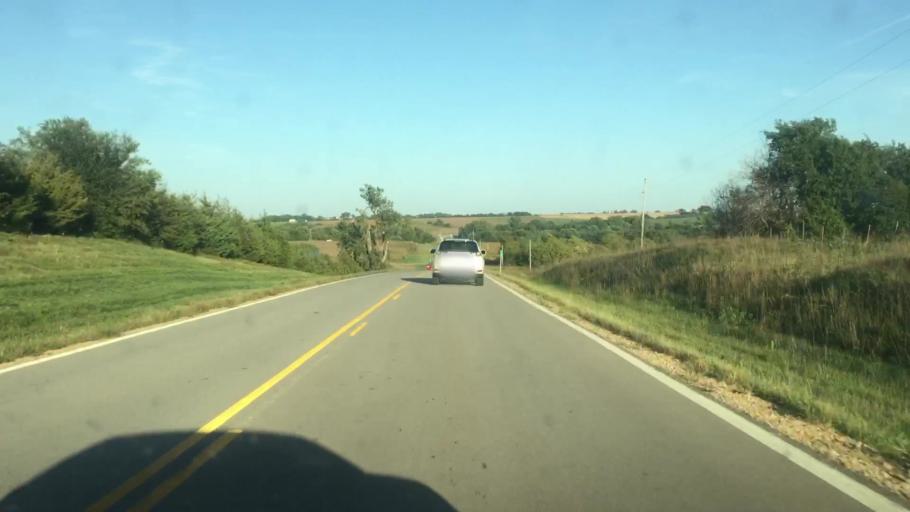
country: US
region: Kansas
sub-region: Brown County
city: Horton
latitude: 39.5874
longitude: -95.5437
